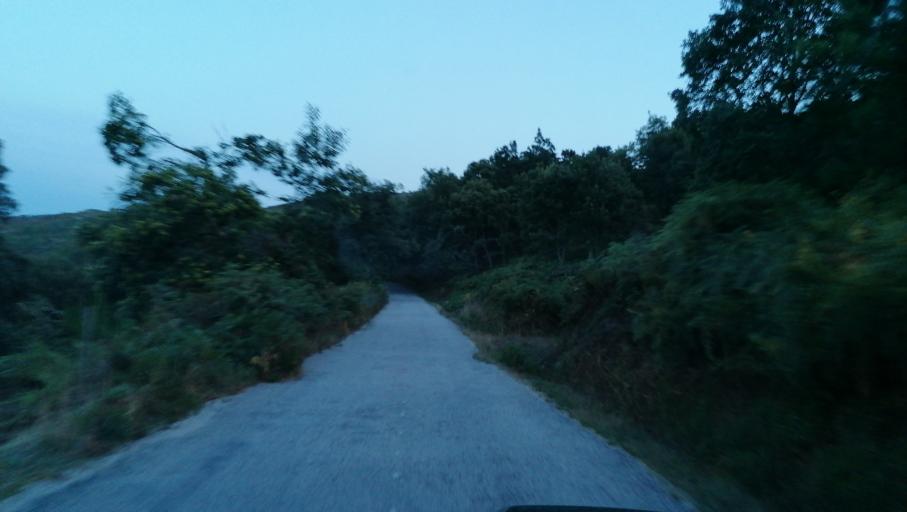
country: PT
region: Vila Real
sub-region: Vila Pouca de Aguiar
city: Vila Pouca de Aguiar
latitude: 41.5584
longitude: -7.6580
